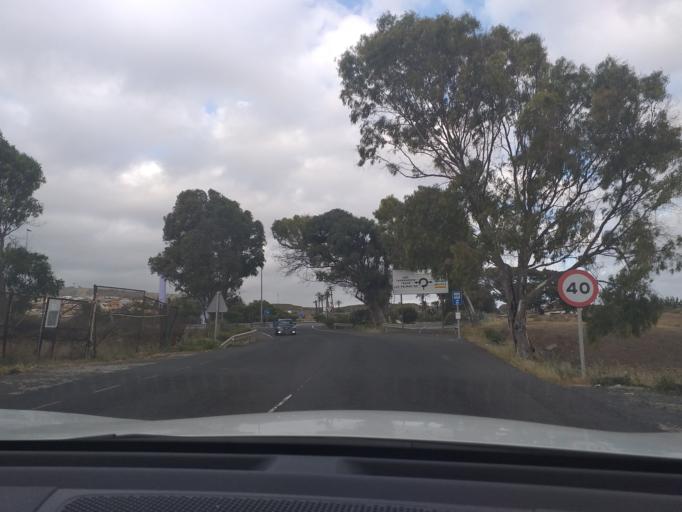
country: ES
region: Canary Islands
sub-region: Provincia de Las Palmas
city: Arucas
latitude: 28.1044
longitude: -15.4872
